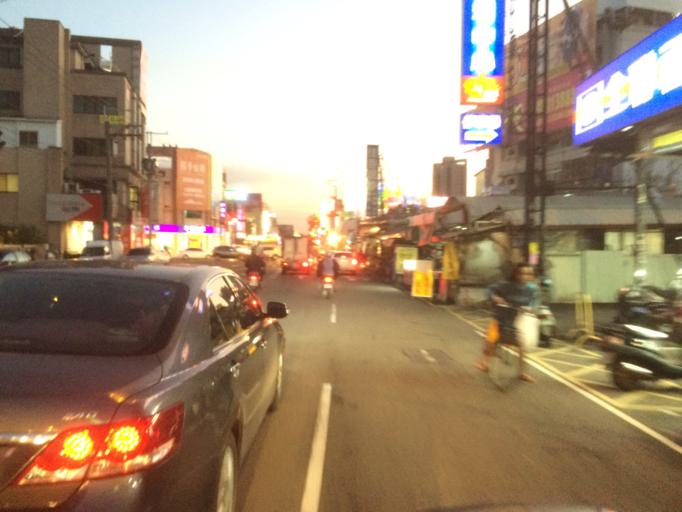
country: TW
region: Taiwan
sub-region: Taichung City
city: Taichung
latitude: 24.1765
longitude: 120.7192
